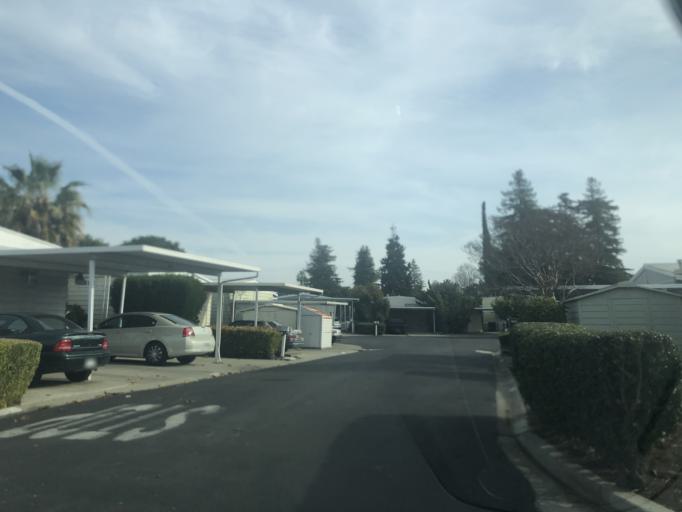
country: US
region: California
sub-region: Contra Costa County
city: Concord
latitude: 38.0009
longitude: -122.0475
